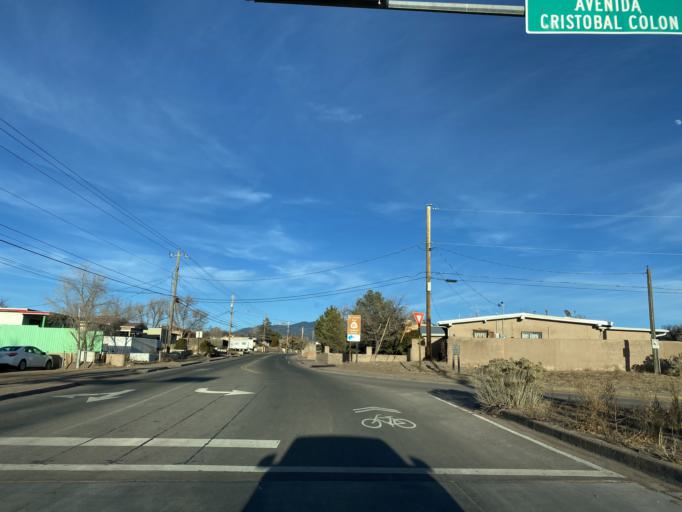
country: US
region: New Mexico
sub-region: Santa Fe County
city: Santa Fe
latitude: 35.6781
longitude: -105.9686
